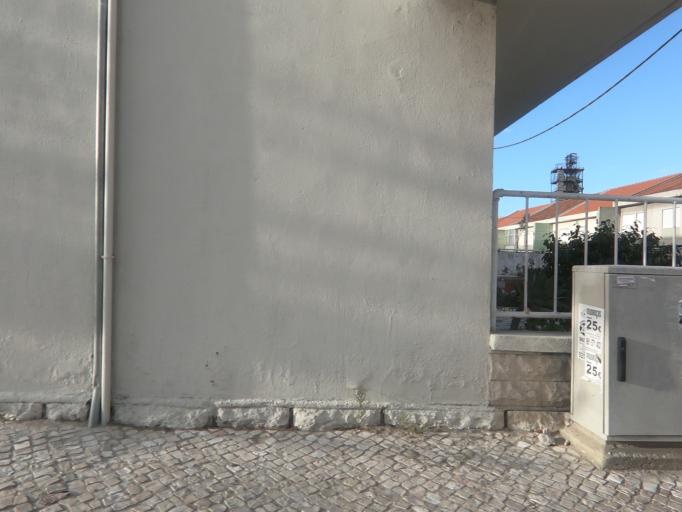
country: PT
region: Setubal
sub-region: Barreiro
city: Barreiro
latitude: 38.6699
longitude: -9.0494
